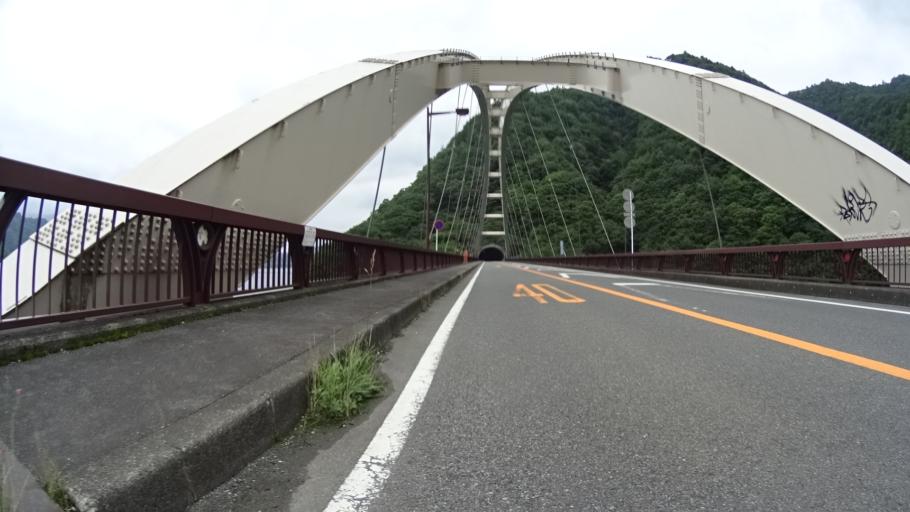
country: JP
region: Kanagawa
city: Atsugi
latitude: 35.5194
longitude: 139.2410
